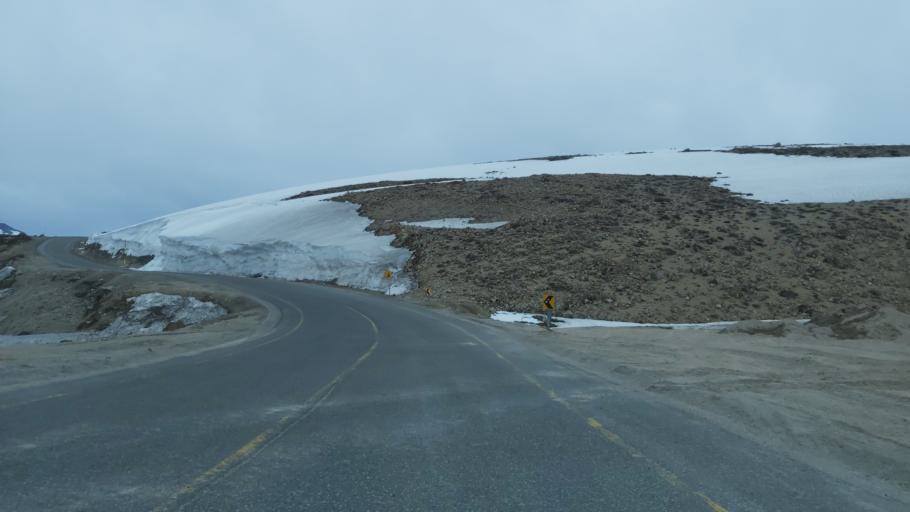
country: CL
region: Maule
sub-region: Provincia de Linares
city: Colbun
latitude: -36.0204
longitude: -70.5271
